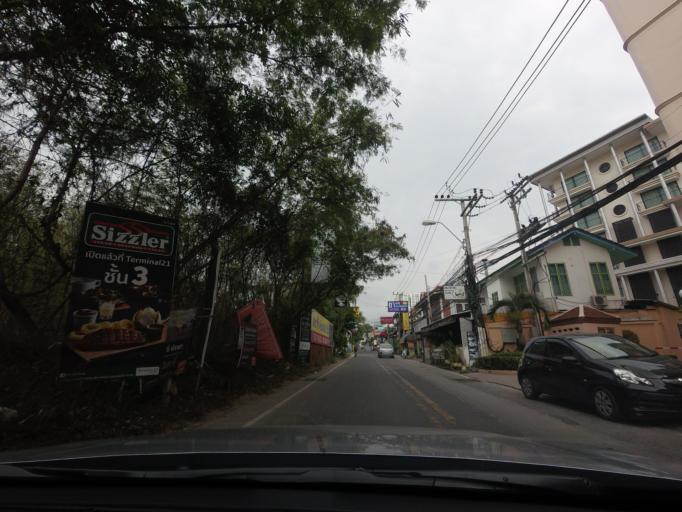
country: TH
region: Chon Buri
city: Phatthaya
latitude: 12.9650
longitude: 100.8863
